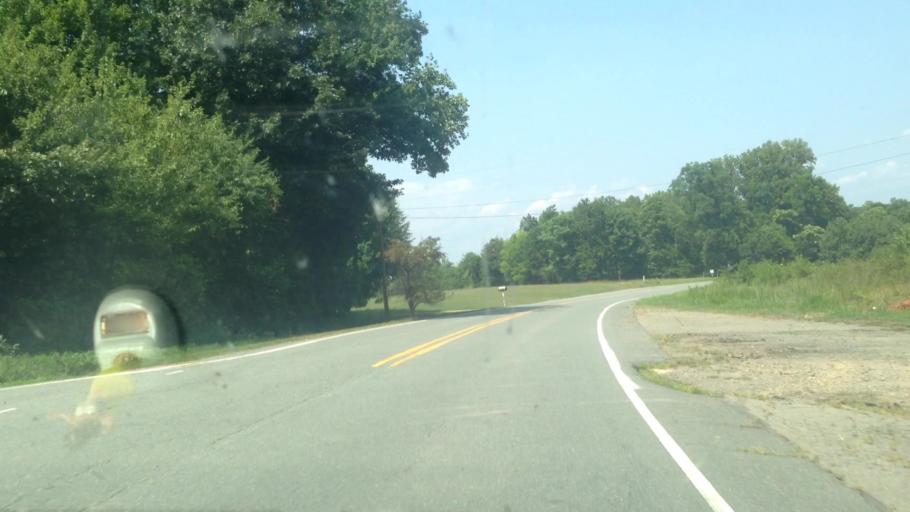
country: US
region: North Carolina
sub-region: Stokes County
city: Walnut Cove
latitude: 36.2990
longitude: -80.0612
